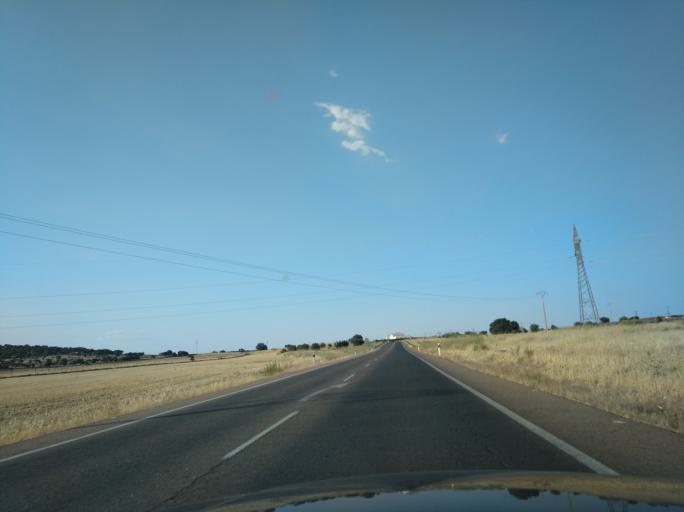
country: ES
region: Extremadura
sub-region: Provincia de Badajoz
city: Olivenza
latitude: 38.7012
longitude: -7.0884
